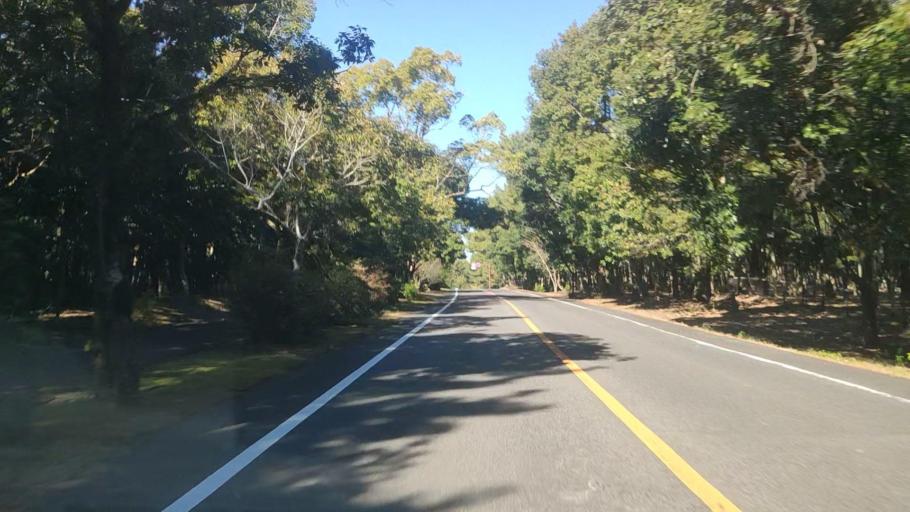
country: JP
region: Miyazaki
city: Miyazaki-shi
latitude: 31.9436
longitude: 131.4648
